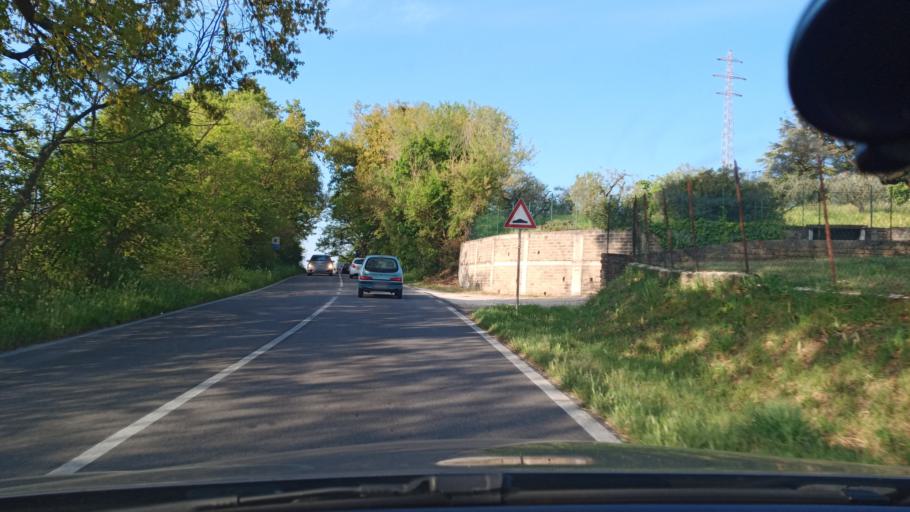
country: IT
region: Latium
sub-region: Citta metropolitana di Roma Capitale
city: Fiano Romano
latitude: 42.1849
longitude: 12.6374
